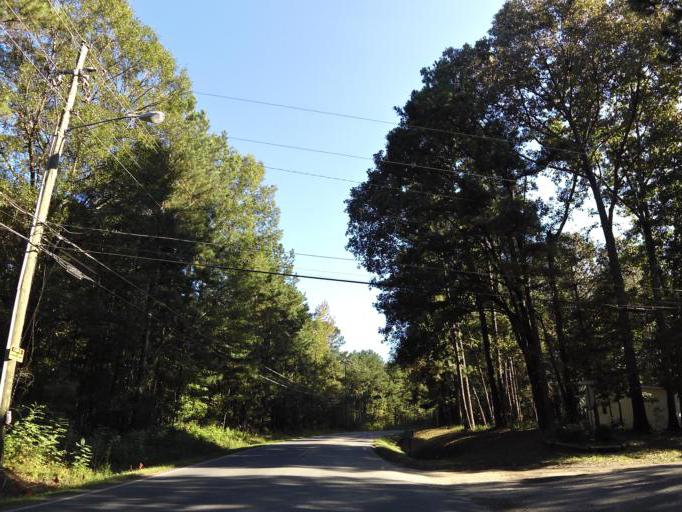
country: US
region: Georgia
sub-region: Cobb County
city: Acworth
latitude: 34.1259
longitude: -84.6804
